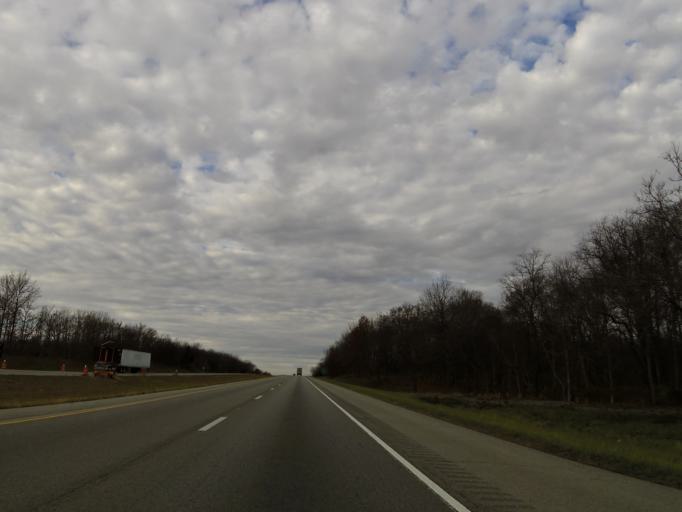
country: US
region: Illinois
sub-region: Jefferson County
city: Mount Vernon
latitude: 38.3622
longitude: -89.0470
